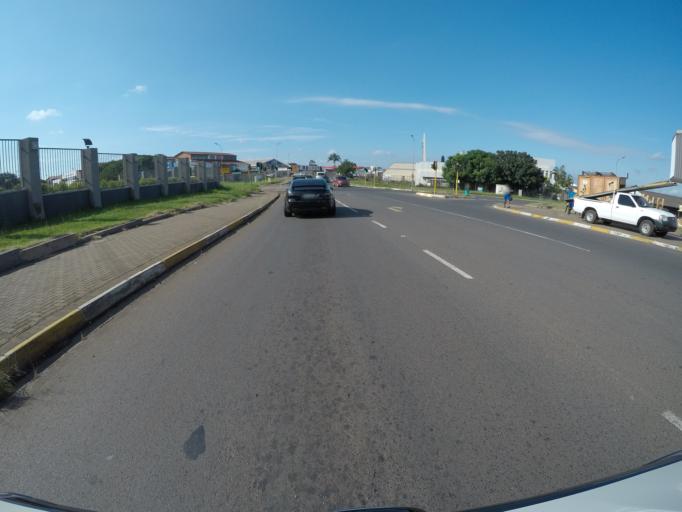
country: ZA
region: KwaZulu-Natal
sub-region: uThungulu District Municipality
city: Empangeni
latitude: -28.7688
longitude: 31.9057
